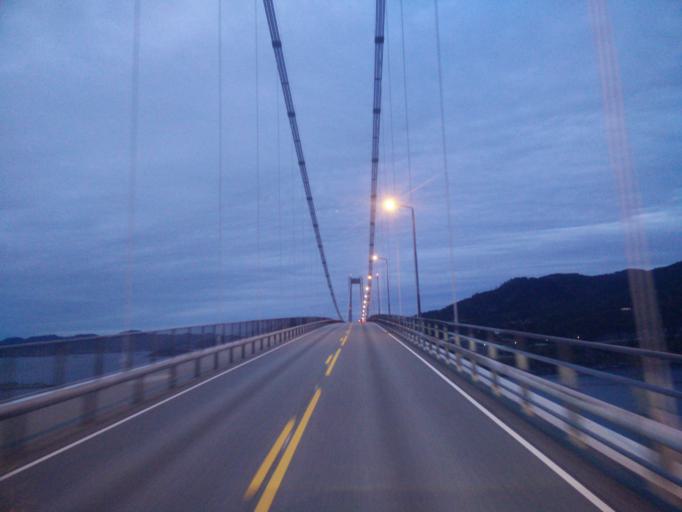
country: NO
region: More og Romsdal
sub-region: Gjemnes
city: Batnfjordsora
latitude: 62.9693
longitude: 7.7760
